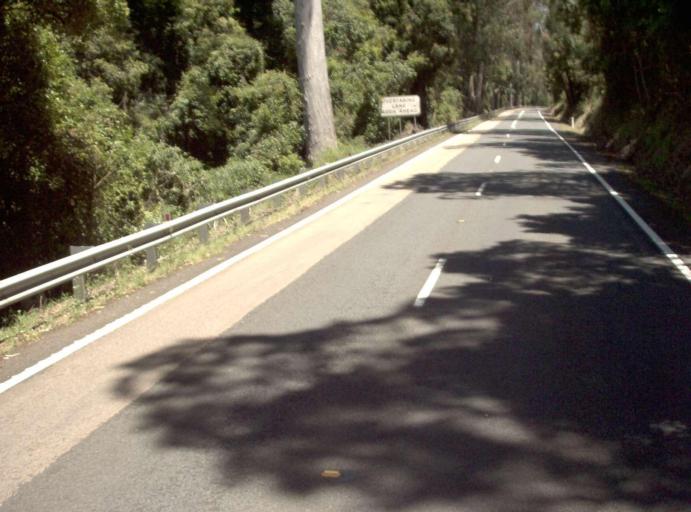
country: AU
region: Victoria
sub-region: East Gippsland
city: Lakes Entrance
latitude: -37.8058
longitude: 148.0415
